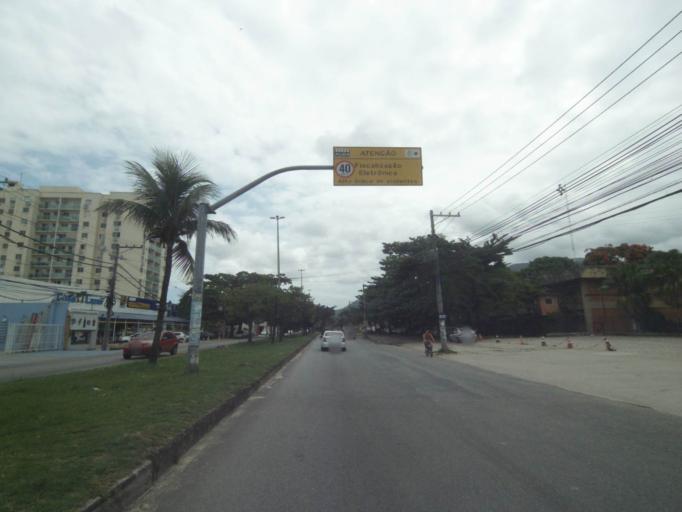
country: BR
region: Rio de Janeiro
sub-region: Nilopolis
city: Nilopolis
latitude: -22.9608
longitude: -43.3929
